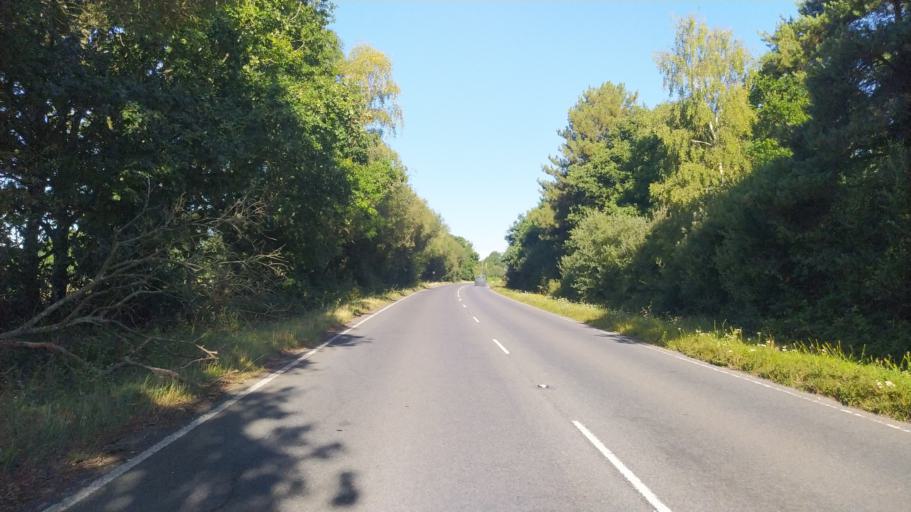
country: GB
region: England
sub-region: Hampshire
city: Cadnam
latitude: 50.9155
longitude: -1.5565
